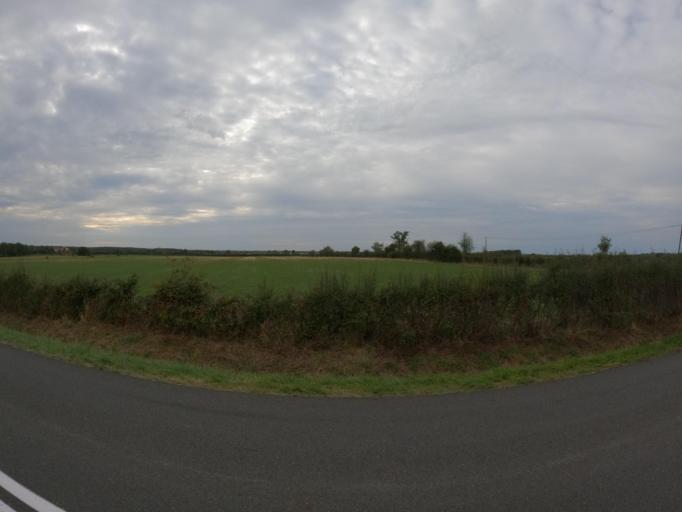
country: FR
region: Poitou-Charentes
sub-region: Departement de la Vienne
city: Saulge
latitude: 46.3750
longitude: 0.8441
